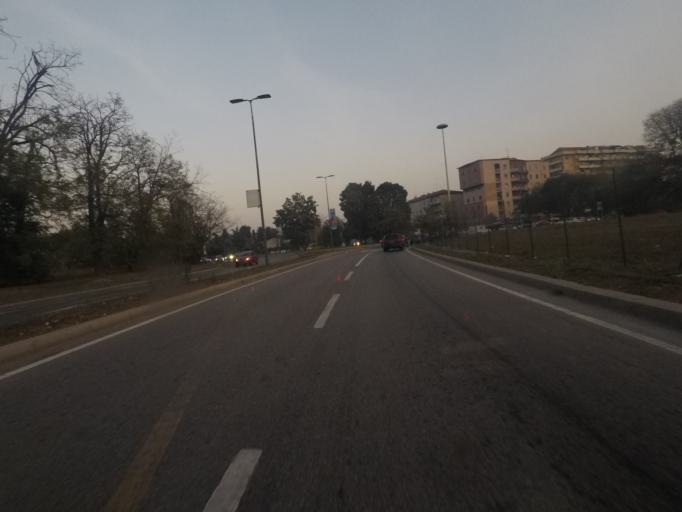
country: IT
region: Lombardy
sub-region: Citta metropolitana di Milano
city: Cologno Monzese
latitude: 45.5131
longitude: 9.2661
